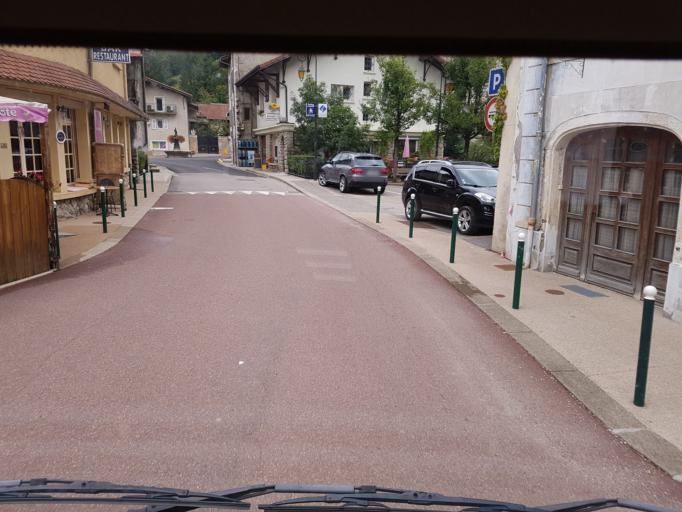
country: FR
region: Rhone-Alpes
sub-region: Departement de l'Ain
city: Poncin
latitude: 46.0802
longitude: 5.4656
